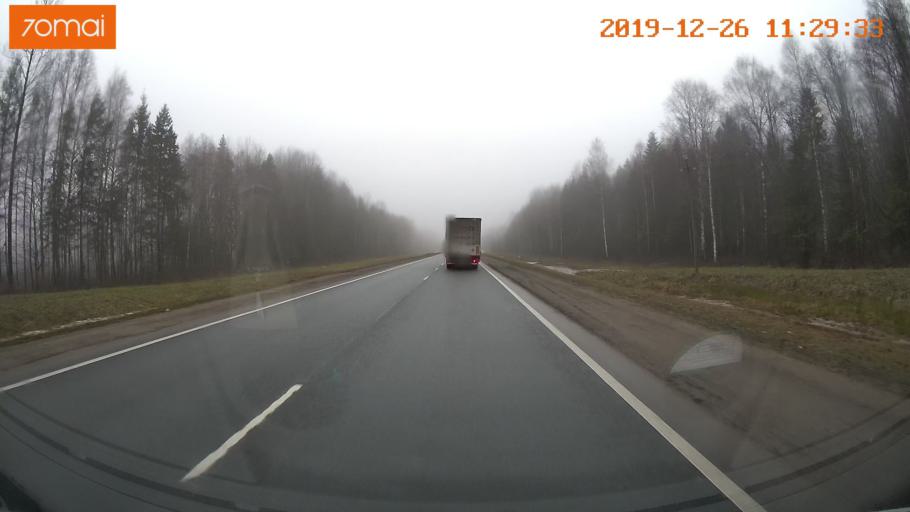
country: RU
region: Vologda
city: Chebsara
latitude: 59.1608
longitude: 38.7924
